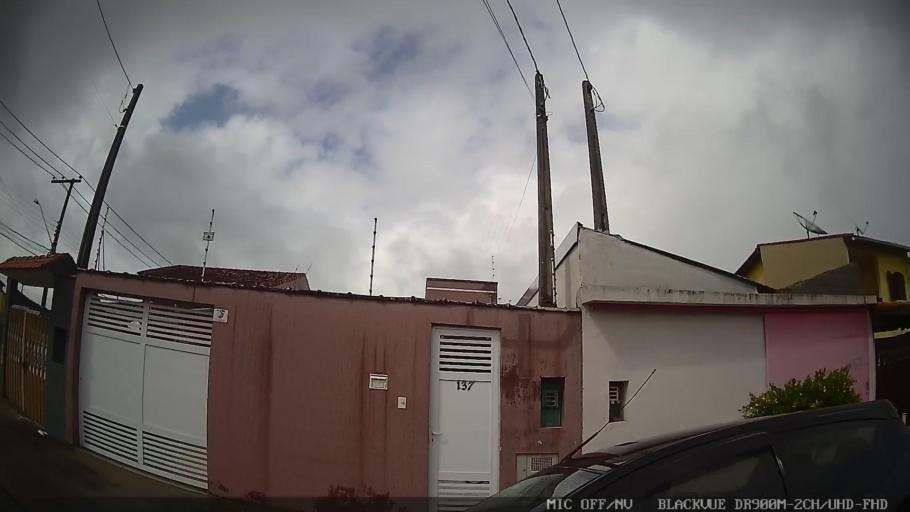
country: BR
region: Sao Paulo
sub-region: Itanhaem
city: Itanhaem
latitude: -24.1913
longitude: -46.8256
